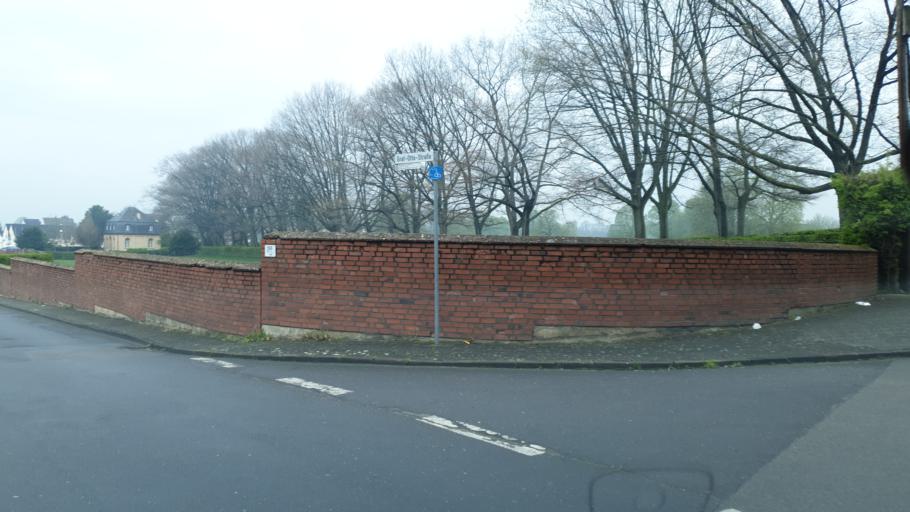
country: DE
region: North Rhine-Westphalia
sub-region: Regierungsbezirk Koln
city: Bergheim
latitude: 50.9427
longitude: 6.6820
